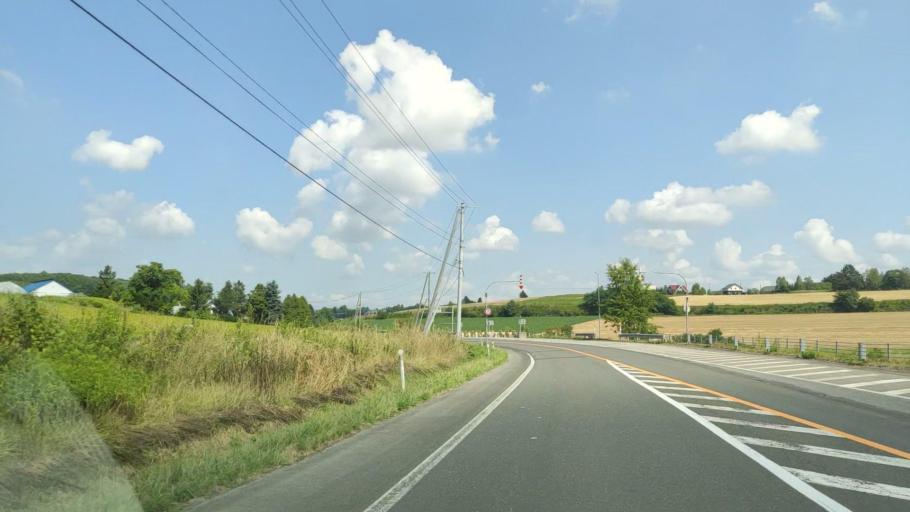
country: JP
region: Hokkaido
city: Shimo-furano
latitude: 43.5345
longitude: 142.4407
